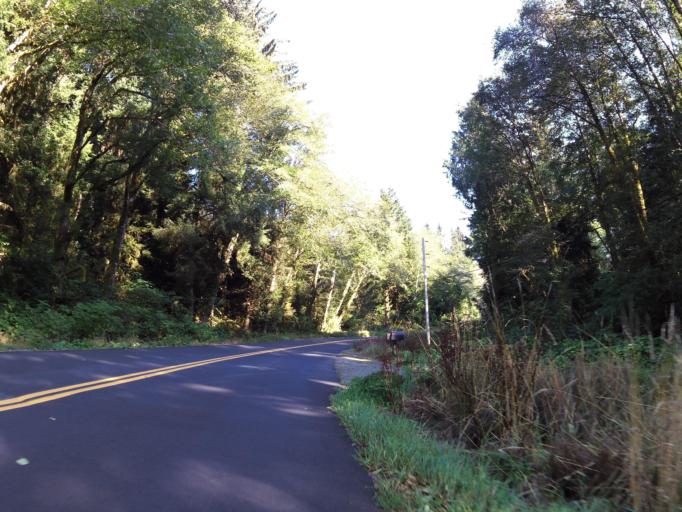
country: US
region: Oregon
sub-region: Lincoln County
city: Rose Lodge
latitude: 45.0800
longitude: -123.9423
